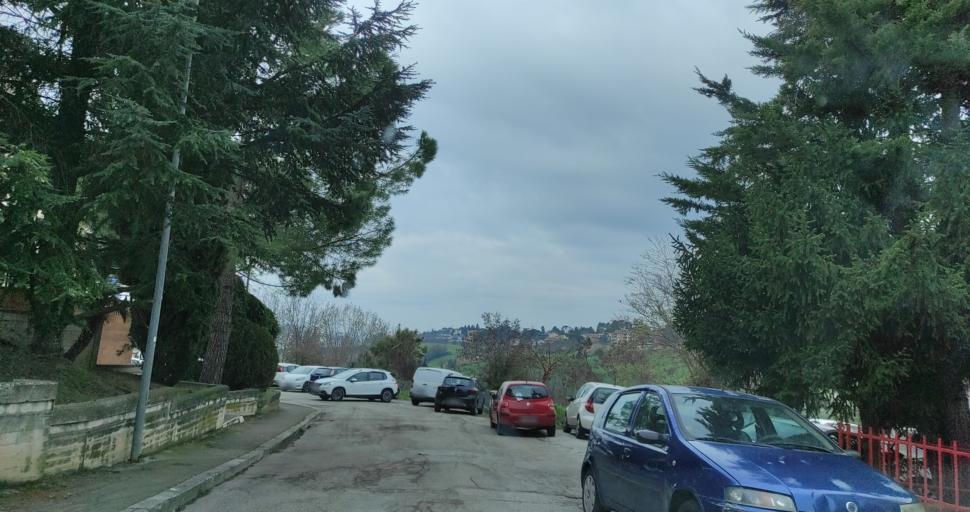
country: IT
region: The Marches
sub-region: Provincia di Macerata
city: Macerata
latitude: 43.2955
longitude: 13.4336
